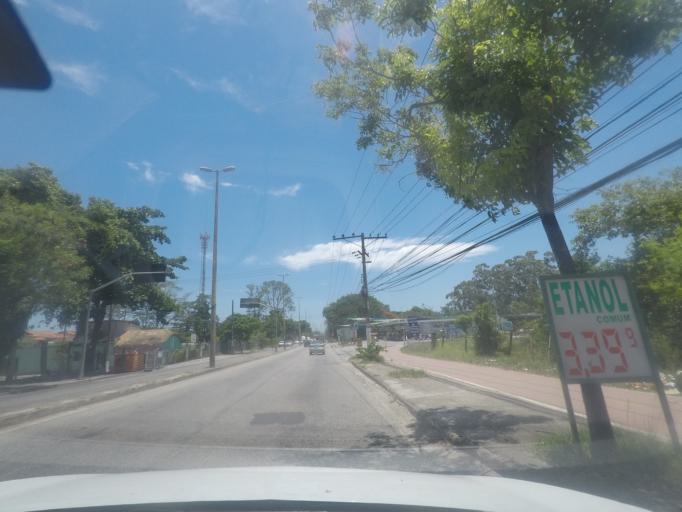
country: BR
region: Rio de Janeiro
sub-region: Itaguai
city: Itaguai
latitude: -22.9039
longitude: -43.6828
